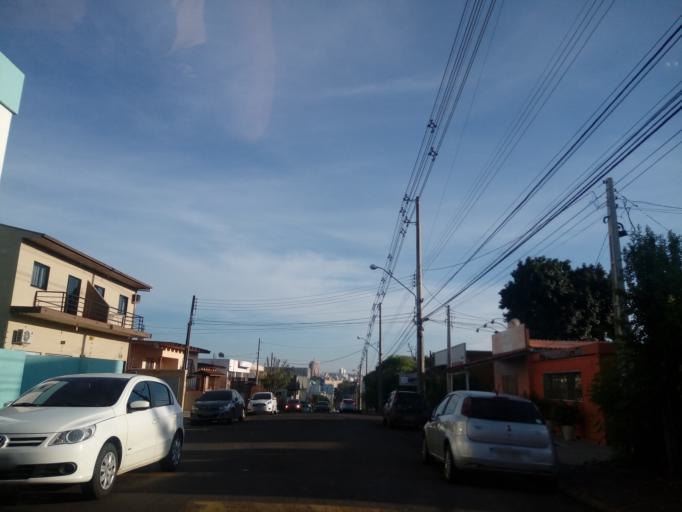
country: BR
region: Santa Catarina
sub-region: Chapeco
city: Chapeco
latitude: -27.1029
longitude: -52.6214
